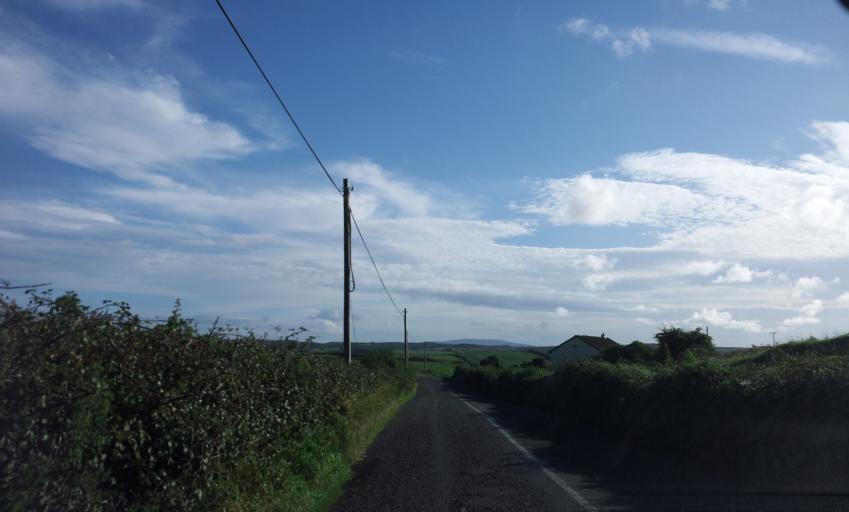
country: IE
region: Munster
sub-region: An Clar
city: Ennis
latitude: 52.9915
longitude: -9.1343
